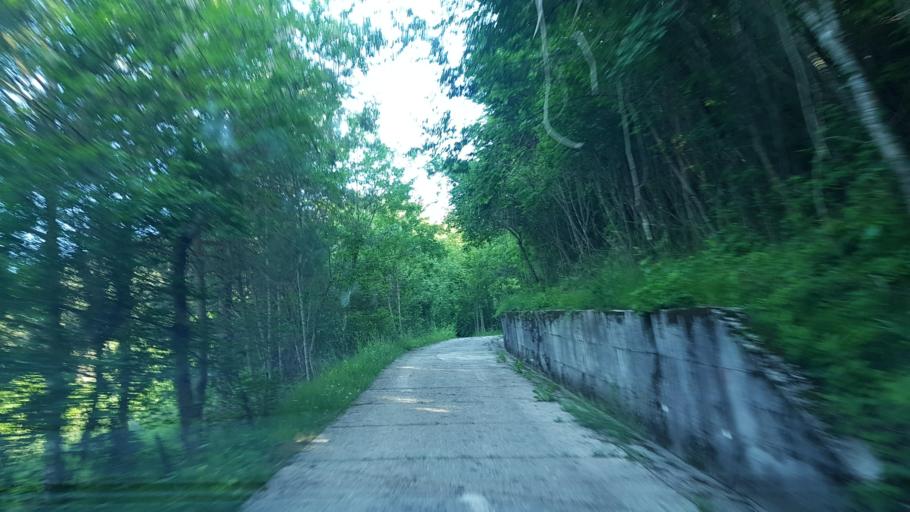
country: IT
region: Friuli Venezia Giulia
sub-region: Provincia di Udine
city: Moggio di Sotto
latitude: 46.4111
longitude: 13.1870
